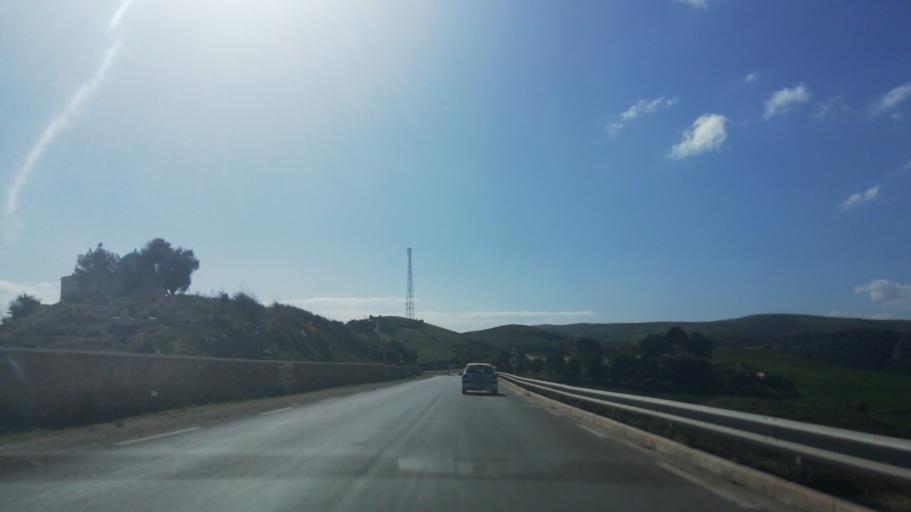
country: DZ
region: Relizane
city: Relizane
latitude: 36.0830
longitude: 0.4992
